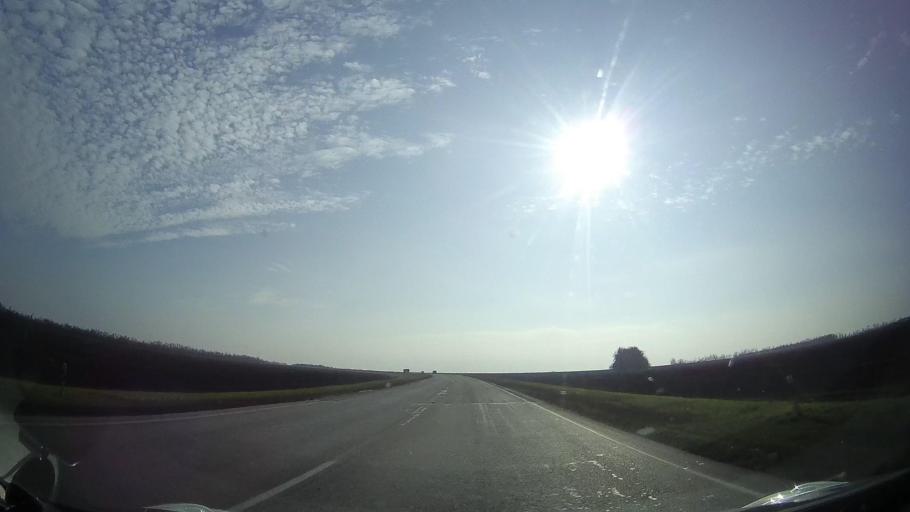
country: RU
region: Rostov
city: Tselina
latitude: 46.5189
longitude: 40.9938
